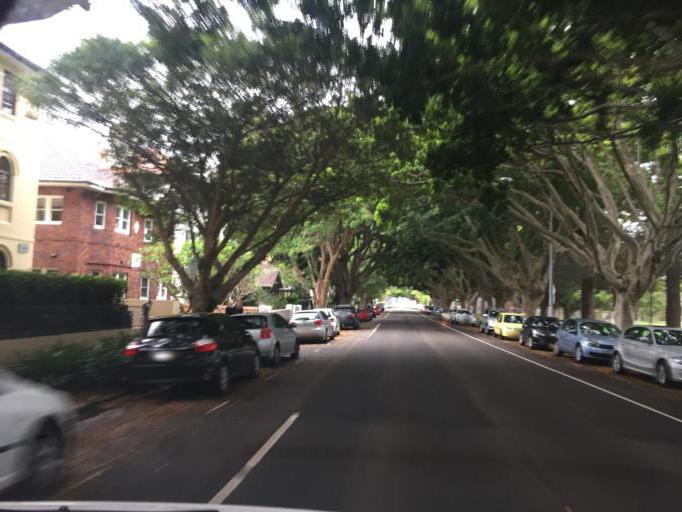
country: AU
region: New South Wales
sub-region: Woollahra
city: Bellevue Hill
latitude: -33.8750
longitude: 151.2602
